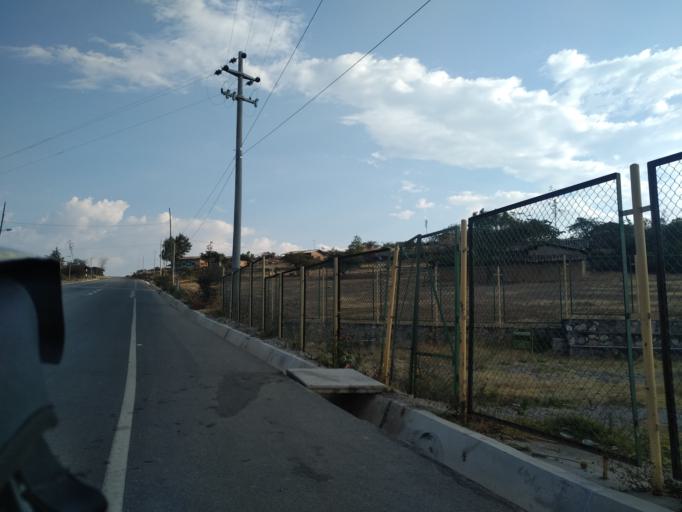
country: PE
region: Cajamarca
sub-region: San Marcos
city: La Grama
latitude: -7.3983
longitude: -78.1256
